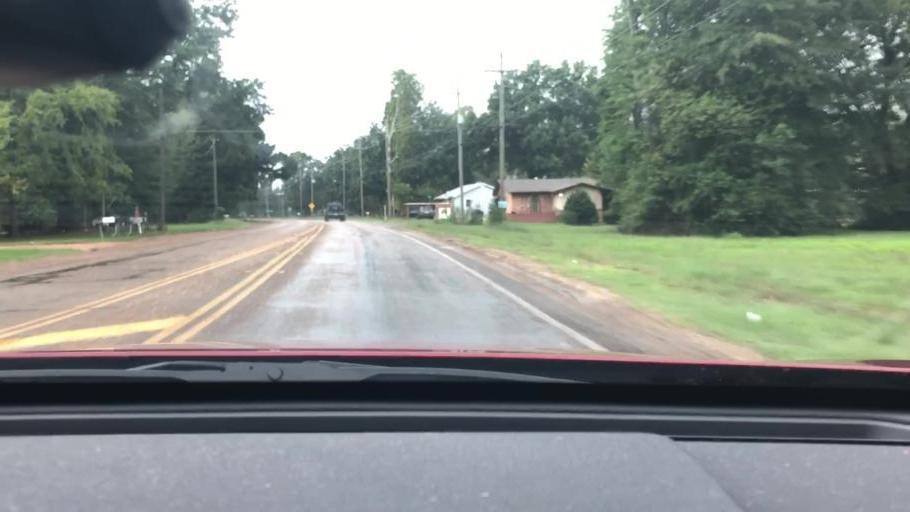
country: US
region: Texas
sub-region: Bowie County
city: Nash
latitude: 33.4425
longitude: -94.1321
